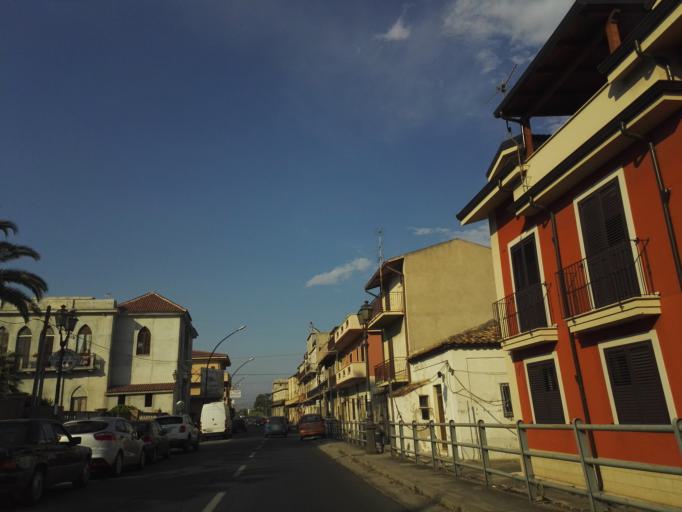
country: IT
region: Calabria
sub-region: Provincia di Reggio Calabria
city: Siderno
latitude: 38.2737
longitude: 16.3042
